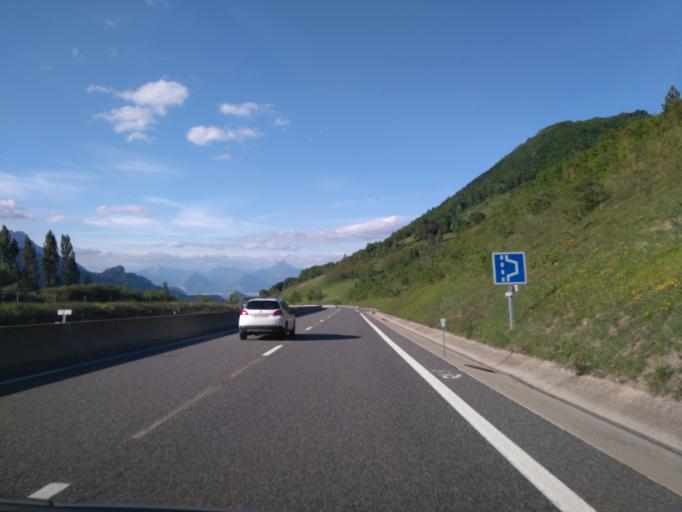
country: FR
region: Rhone-Alpes
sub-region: Departement de l'Isere
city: Vif
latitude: 45.0166
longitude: 5.6593
